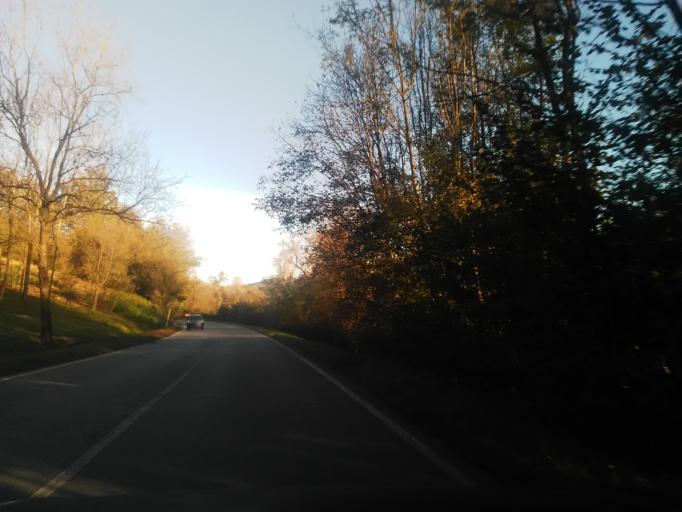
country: IT
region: Piedmont
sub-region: Provincia di Vercelli
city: Roasio
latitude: 45.6137
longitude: 8.2873
